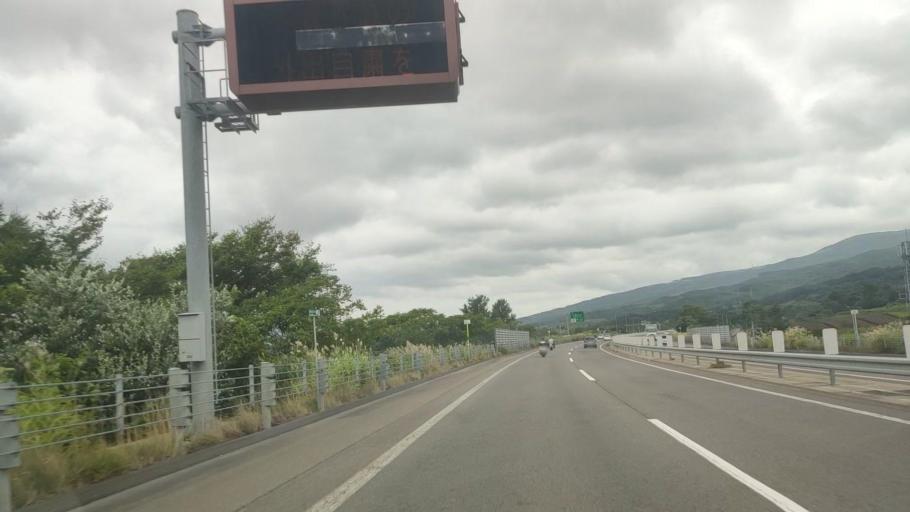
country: JP
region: Hokkaido
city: Nanae
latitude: 41.8630
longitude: 140.7314
